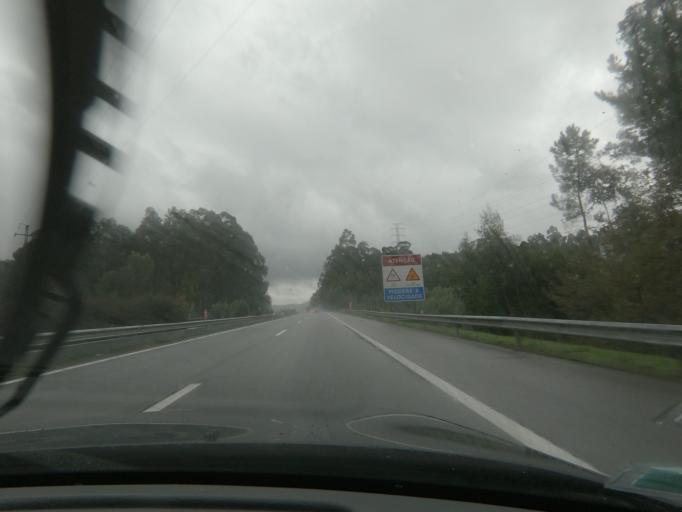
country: PT
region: Porto
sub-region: Paredes
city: Recarei
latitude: 41.1666
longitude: -8.3907
